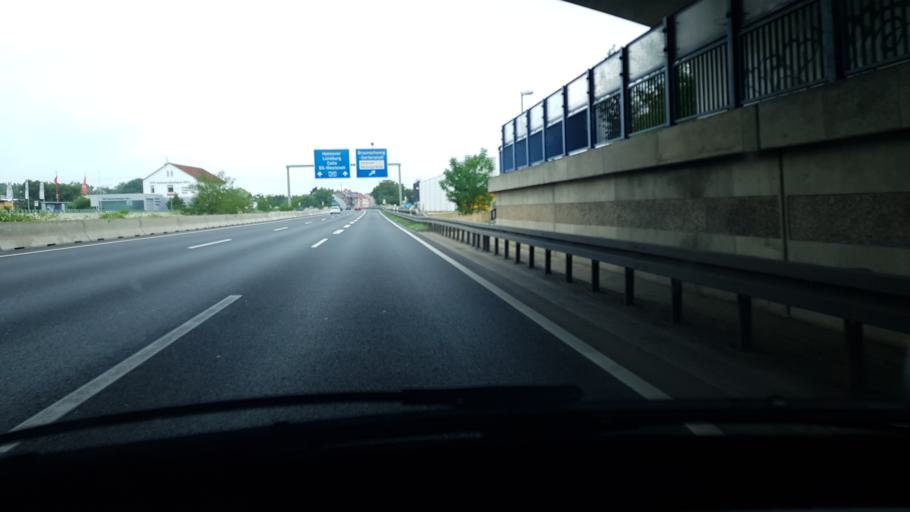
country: DE
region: Lower Saxony
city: Braunschweig
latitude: 52.2405
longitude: 10.5098
